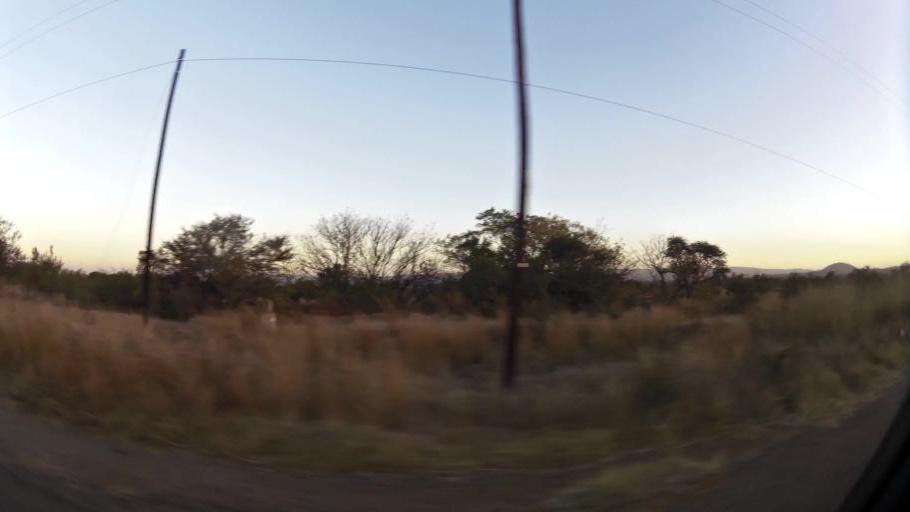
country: ZA
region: North-West
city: Ga-Rankuwa
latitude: -25.6206
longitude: 28.0317
